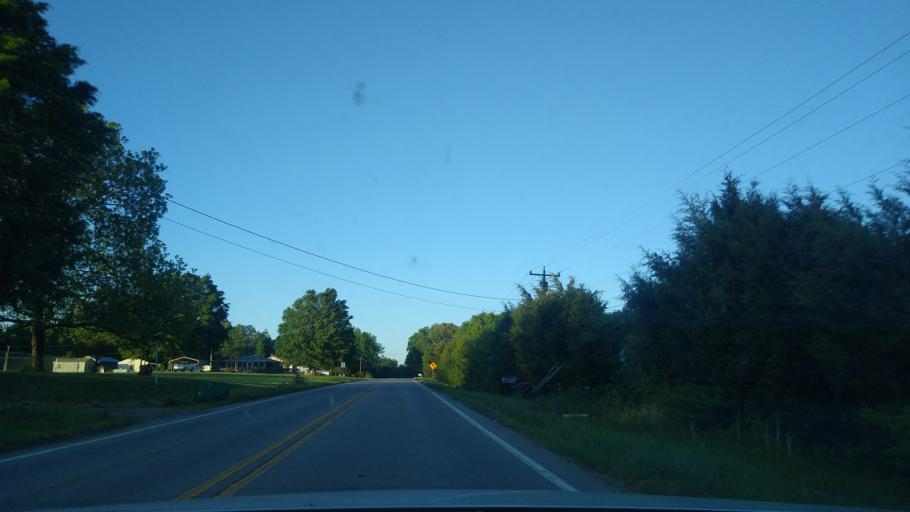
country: US
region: North Carolina
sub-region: Rockingham County
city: Reidsville
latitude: 36.3727
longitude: -79.5968
